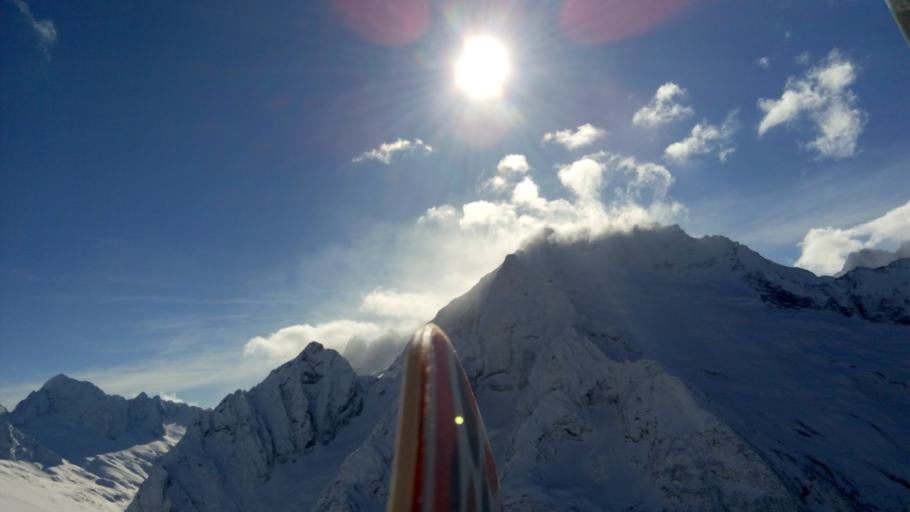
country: RU
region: Karachayevo-Cherkesiya
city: Teberda
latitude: 43.2912
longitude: 41.6633
